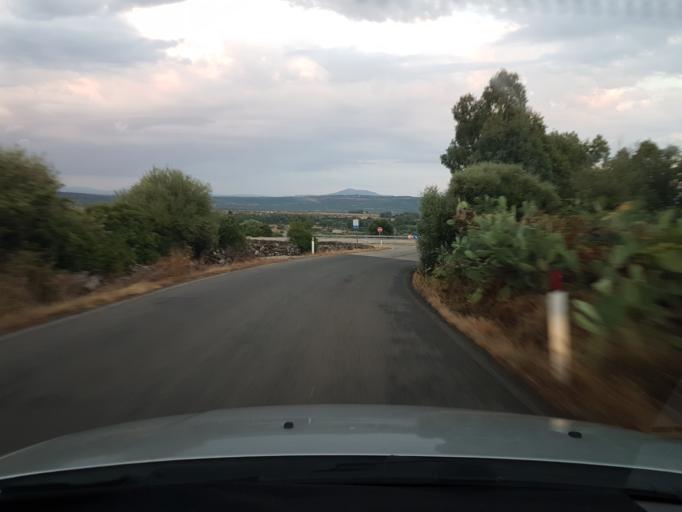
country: IT
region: Sardinia
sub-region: Provincia di Oristano
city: Milis
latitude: 40.0569
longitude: 8.6366
